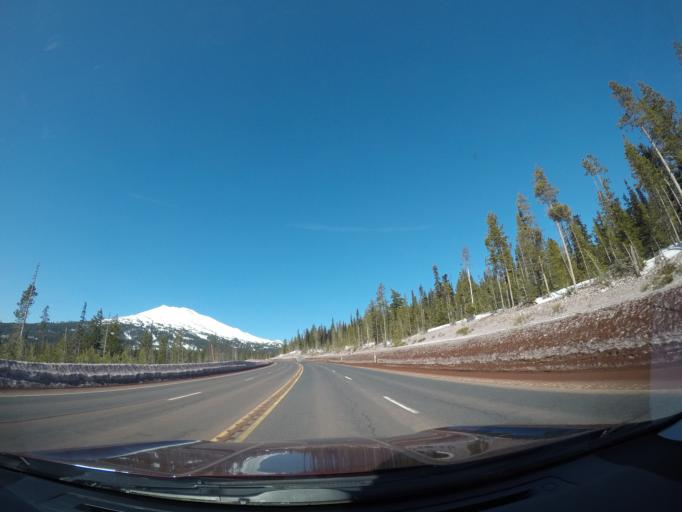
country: US
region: Oregon
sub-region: Deschutes County
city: Sunriver
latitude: 43.9840
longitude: -121.6339
